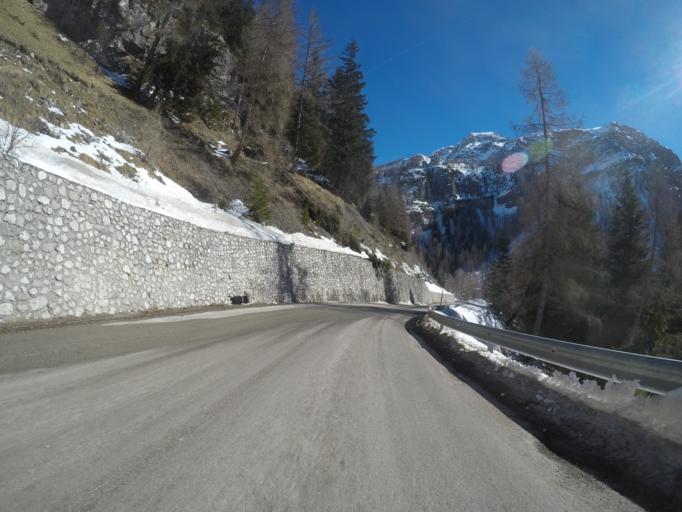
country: IT
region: Veneto
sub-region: Provincia di Belluno
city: Selva di Cadore
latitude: 46.4763
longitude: 12.0347
